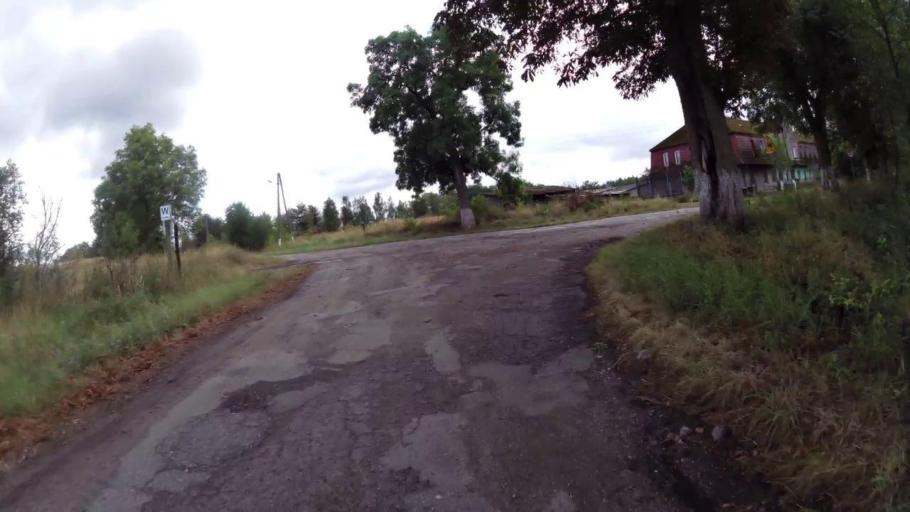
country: PL
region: West Pomeranian Voivodeship
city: Trzcinsko Zdroj
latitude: 52.8871
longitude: 14.7158
